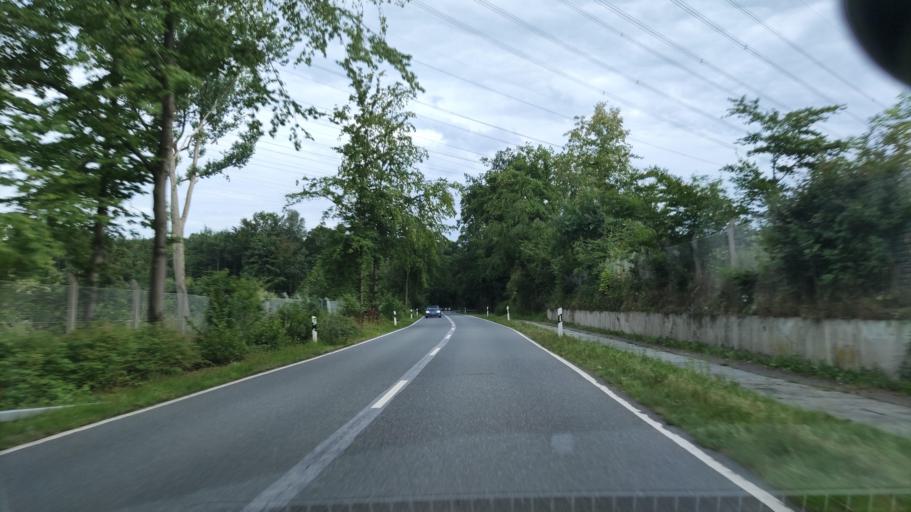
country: DE
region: Lower Saxony
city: Tespe
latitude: 53.4175
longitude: 10.4241
